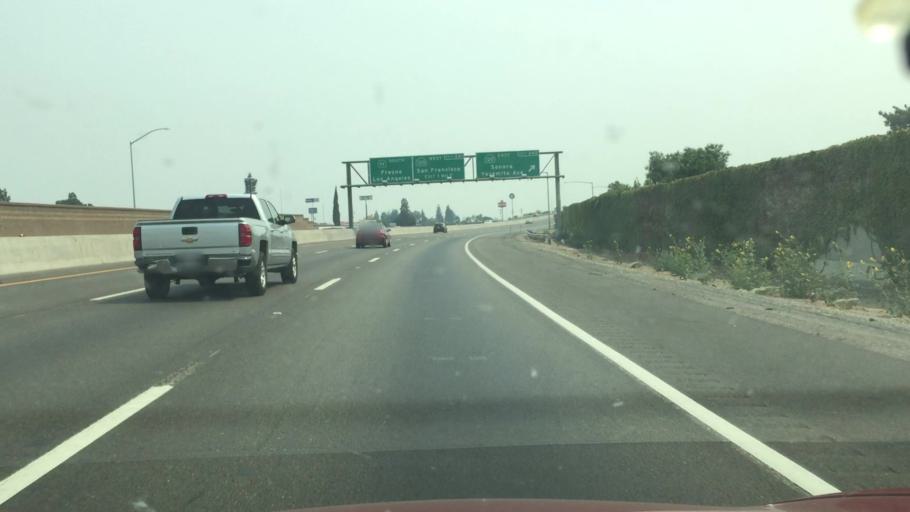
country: US
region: California
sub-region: San Joaquin County
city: Manteca
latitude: 37.8018
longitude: -121.1930
